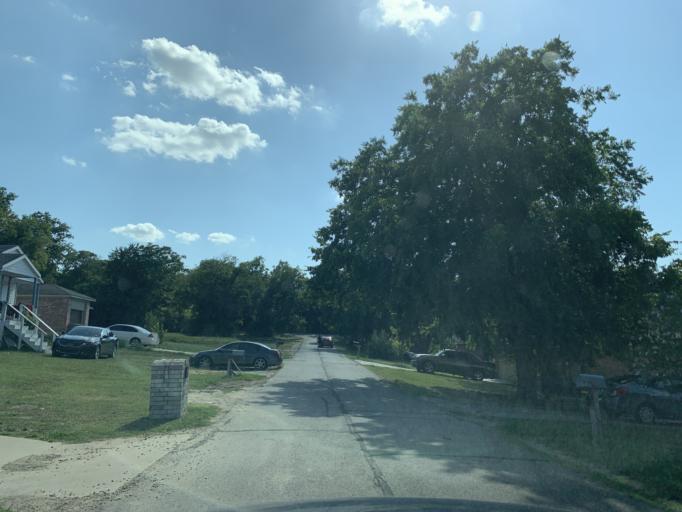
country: US
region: Texas
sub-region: Dallas County
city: Hutchins
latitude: 32.6755
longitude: -96.7790
